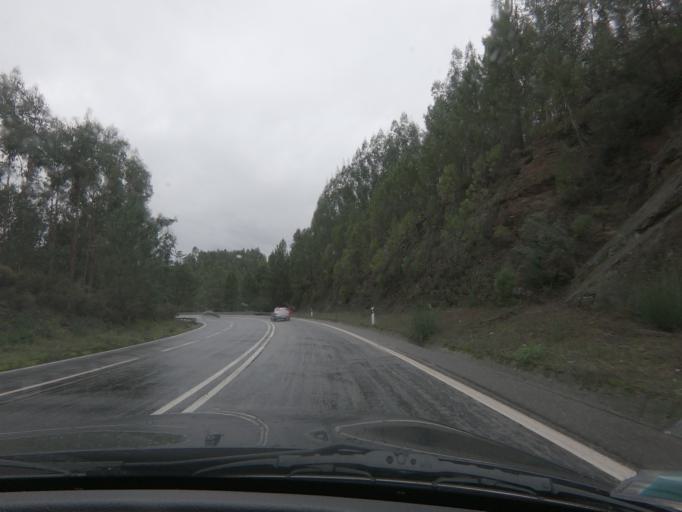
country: PT
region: Porto
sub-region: Amarante
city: Teloes
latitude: 41.3251
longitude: -8.0594
